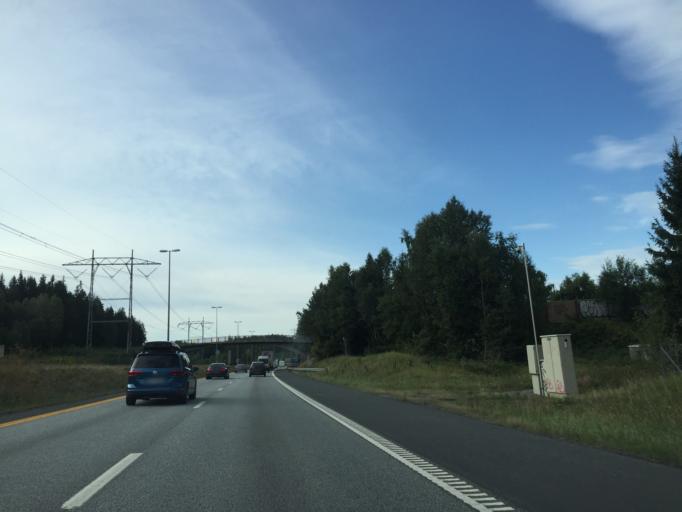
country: NO
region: Akershus
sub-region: Oppegard
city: Kolbotn
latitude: 59.7998
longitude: 10.8429
